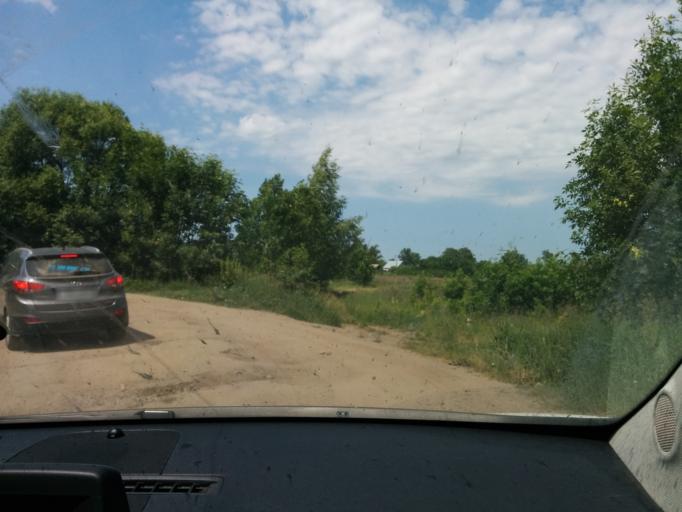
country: RU
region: Tambov
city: Morshansk
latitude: 53.6156
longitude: 41.8319
